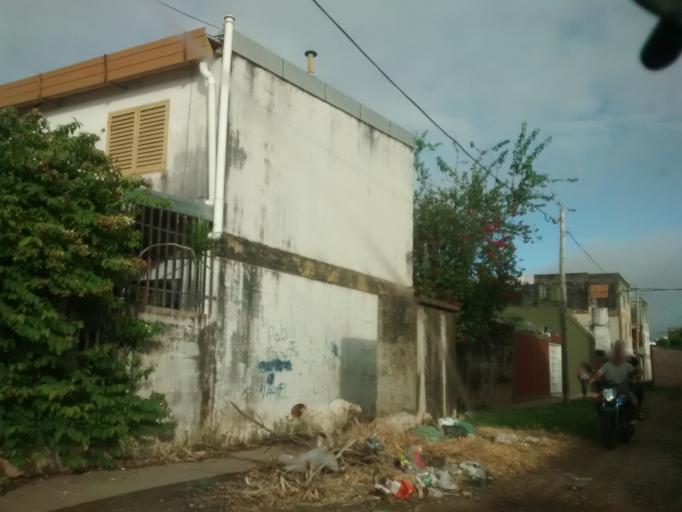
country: AR
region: Chaco
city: Resistencia
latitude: -27.4495
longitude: -59.0136
